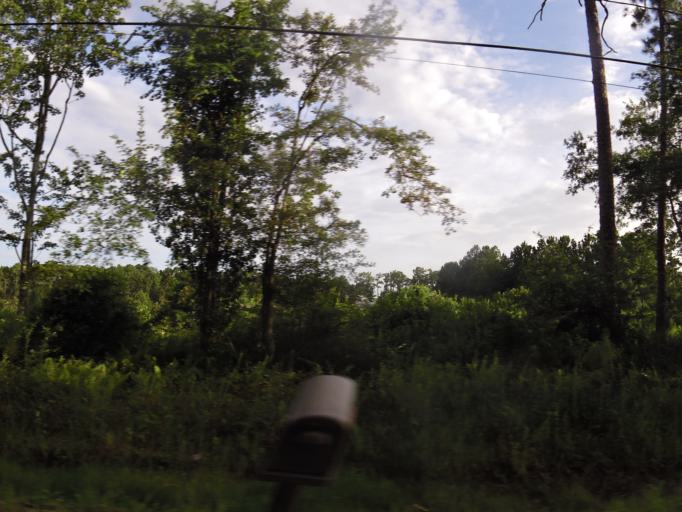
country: US
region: Florida
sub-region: Nassau County
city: Nassau Village-Ratliff
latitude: 30.4161
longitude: -81.7479
